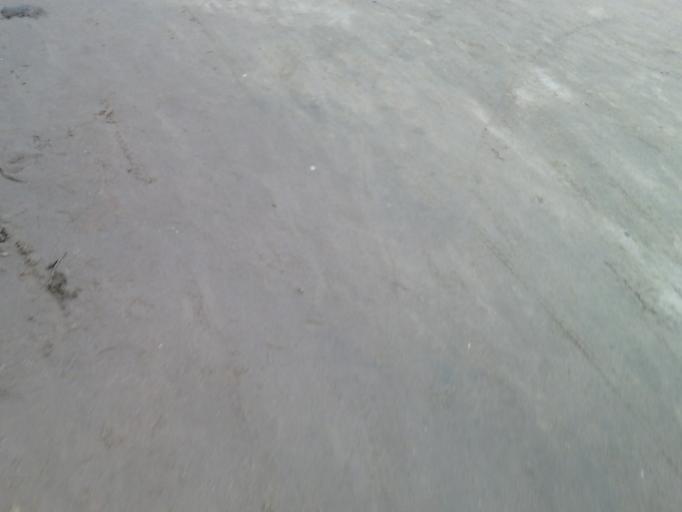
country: BJ
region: Atlantique
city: Abomey-Calavi
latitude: 6.3907
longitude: 2.3617
